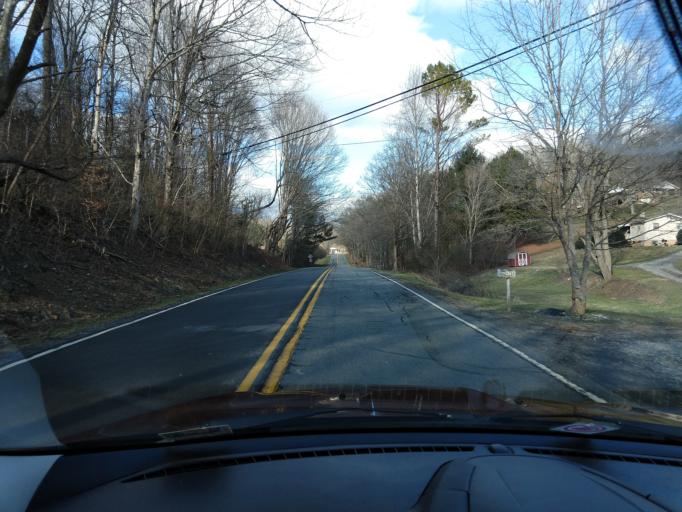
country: US
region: Virginia
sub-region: City of Lexington
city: Lexington
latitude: 37.8251
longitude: -79.4963
